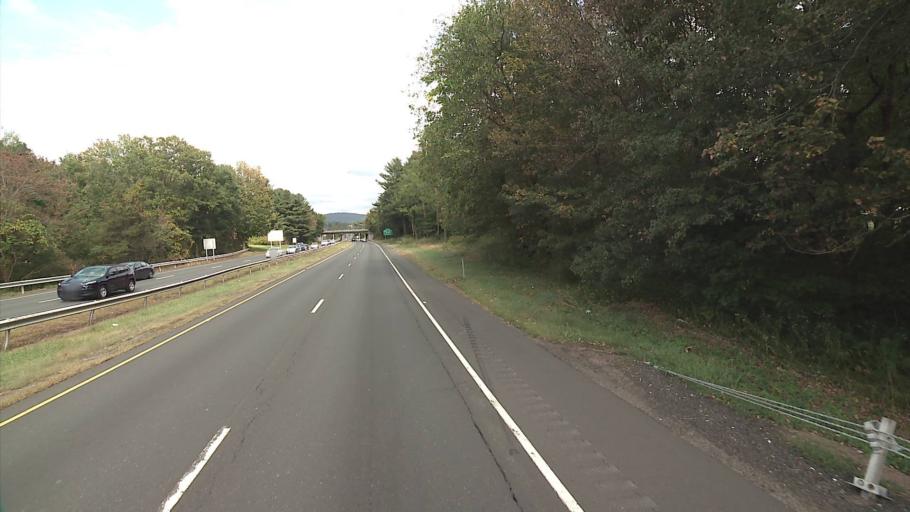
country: US
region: Connecticut
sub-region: New Haven County
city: Meriden
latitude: 41.5148
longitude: -72.7784
